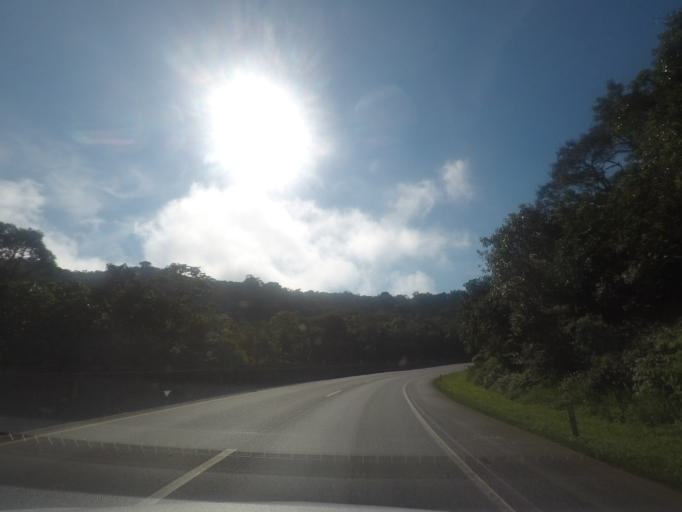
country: BR
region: Parana
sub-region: Piraquara
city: Piraquara
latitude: -25.5915
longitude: -48.8945
